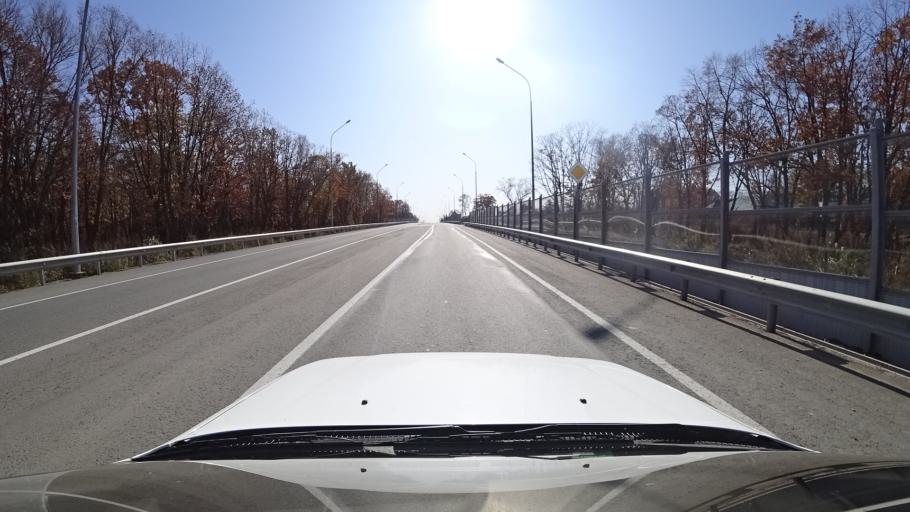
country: RU
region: Primorskiy
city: Dal'nerechensk
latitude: 45.8838
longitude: 133.7299
